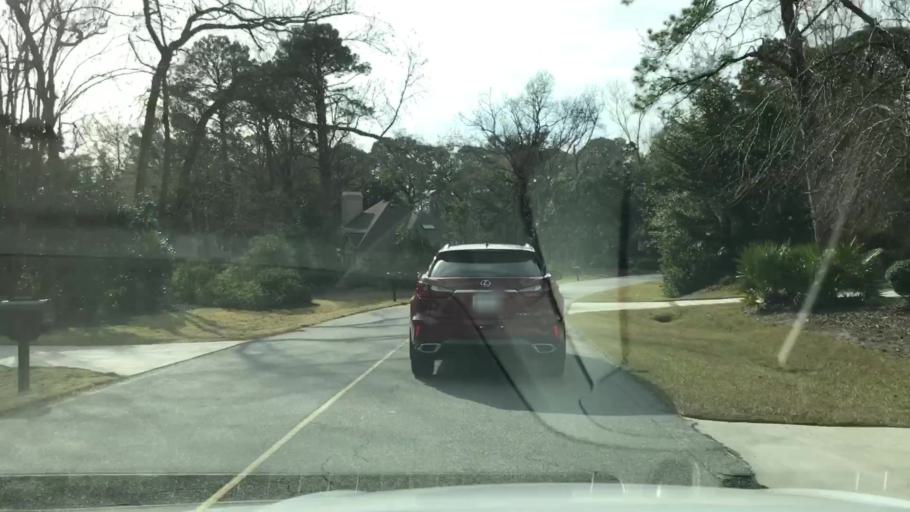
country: US
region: South Carolina
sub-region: Beaufort County
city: Hilton Head Island
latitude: 32.2396
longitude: -80.7130
